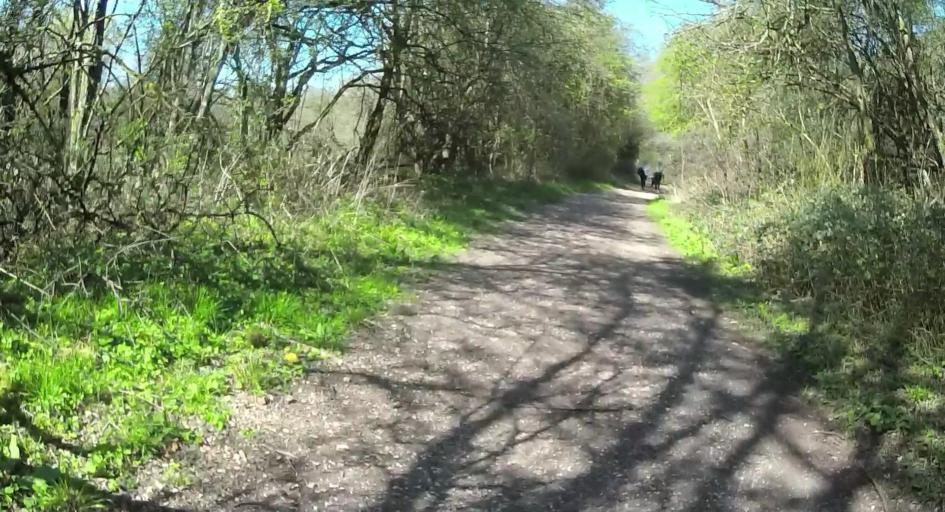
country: GB
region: England
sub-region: Hampshire
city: Romsey
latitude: 51.0877
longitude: -1.5011
